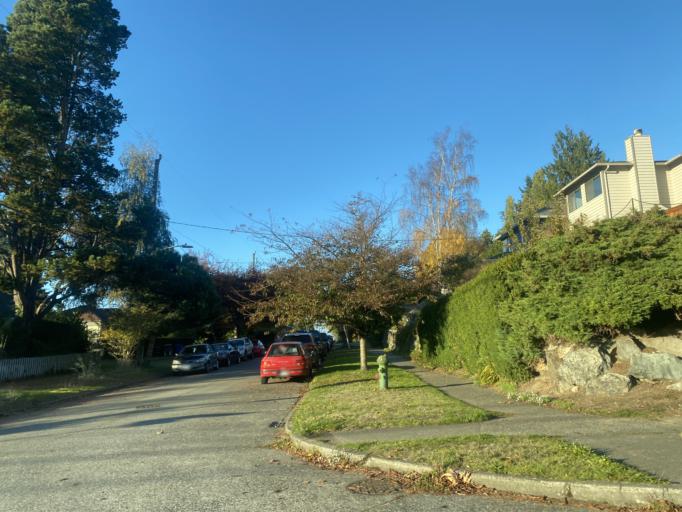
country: US
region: Washington
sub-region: King County
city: Seattle
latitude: 47.6541
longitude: -122.3996
